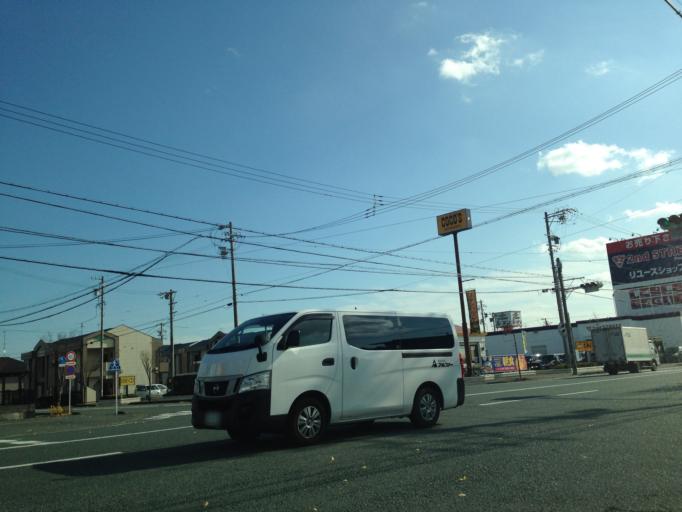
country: JP
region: Shizuoka
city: Fukuroi
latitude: 34.7484
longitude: 137.9101
